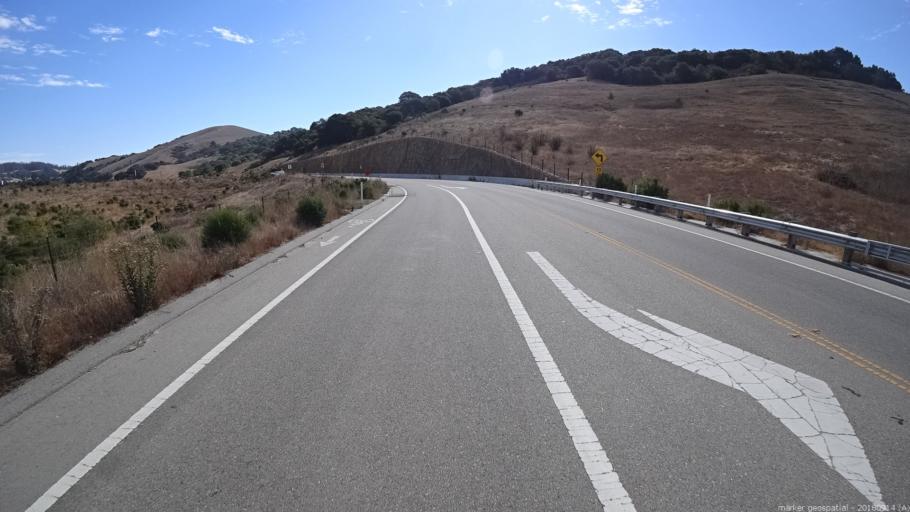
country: US
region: California
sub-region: San Benito County
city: Aromas
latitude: 36.8562
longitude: -121.6284
